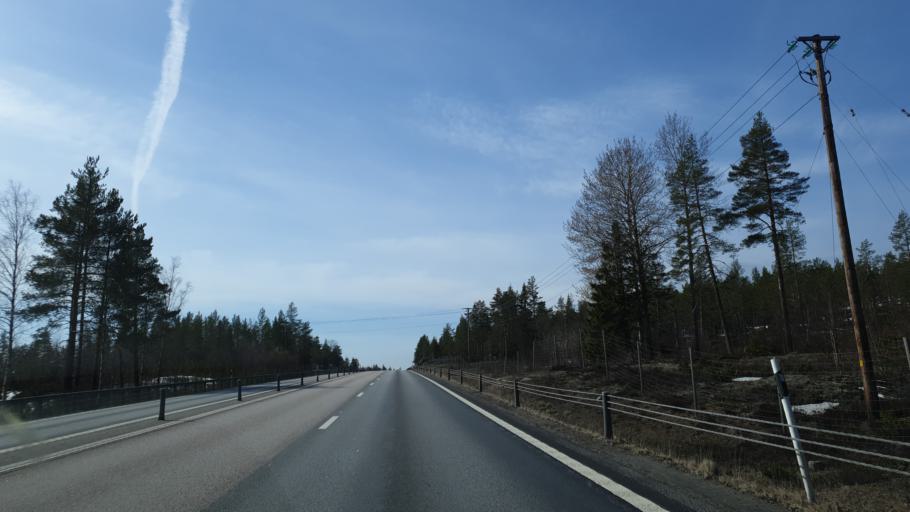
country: SE
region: Vaesterbotten
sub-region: Nordmalings Kommun
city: Nordmaling
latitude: 63.4933
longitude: 19.3179
